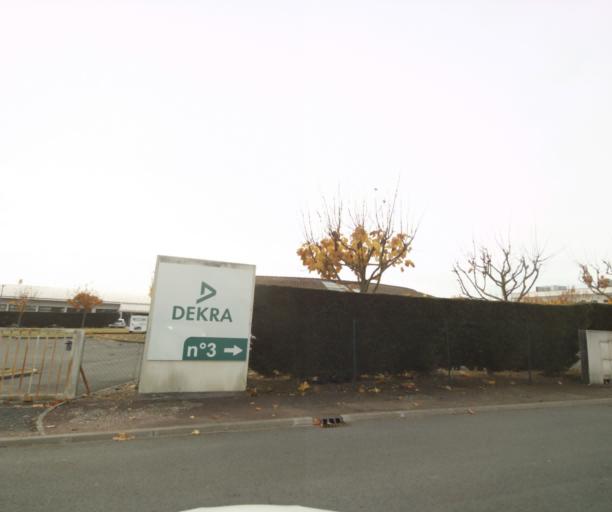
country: FR
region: Poitou-Charentes
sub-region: Departement de la Charente-Maritime
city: Saintes
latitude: 45.7478
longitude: -0.6601
